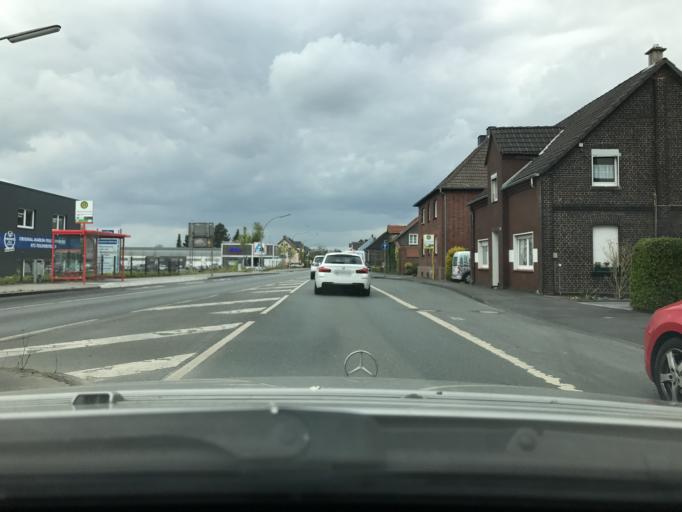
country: DE
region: North Rhine-Westphalia
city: Waltrop
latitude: 51.6055
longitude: 7.3928
